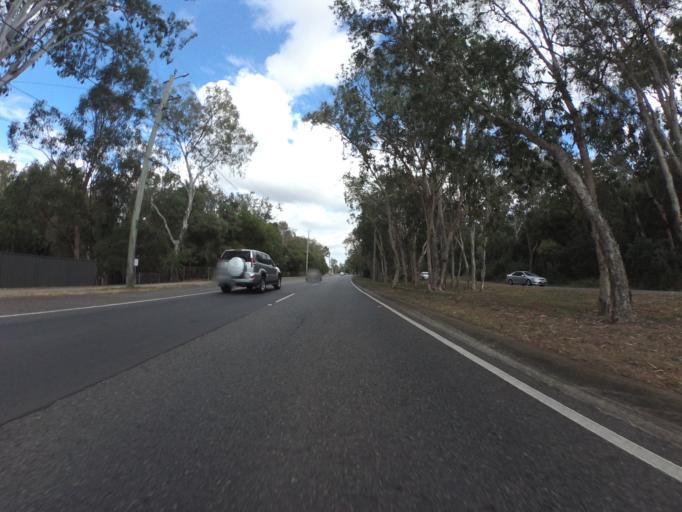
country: AU
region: Queensland
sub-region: Brisbane
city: Wynnum West
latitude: -27.4694
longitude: 153.1364
